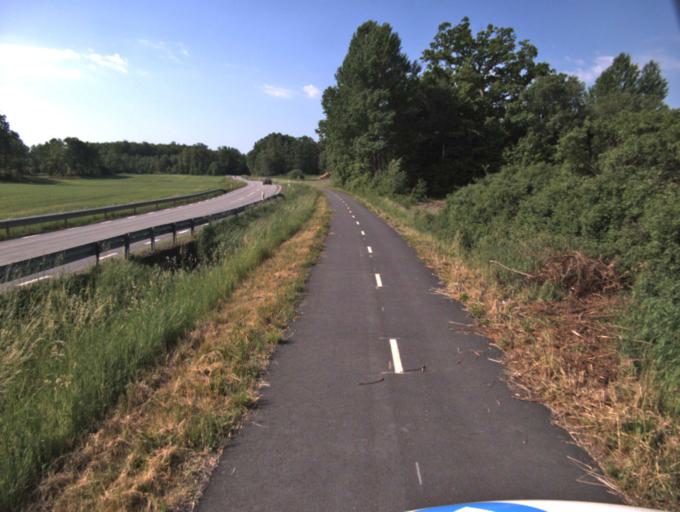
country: SE
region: Skane
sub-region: Kristianstads Kommun
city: Tollarp
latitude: 56.1522
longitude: 14.2627
